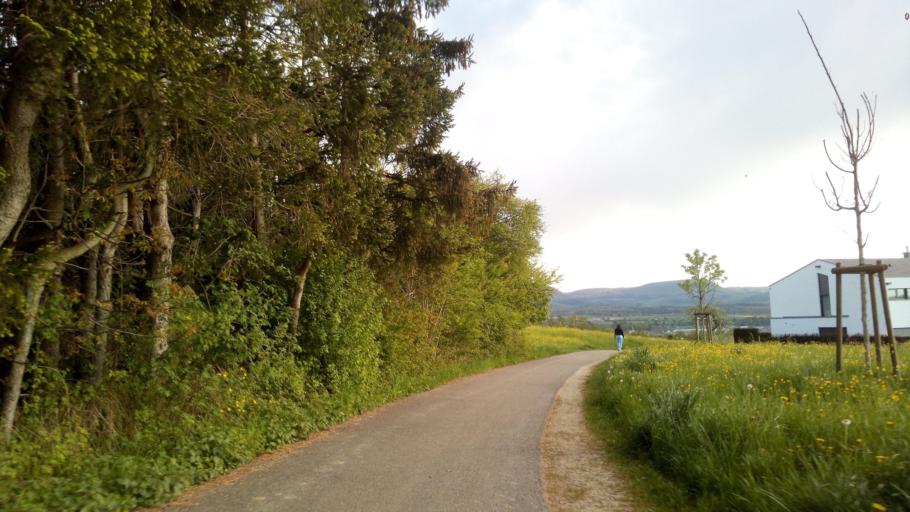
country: DE
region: Baden-Wuerttemberg
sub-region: Regierungsbezirk Stuttgart
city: Salach
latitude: 48.6982
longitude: 9.7515
